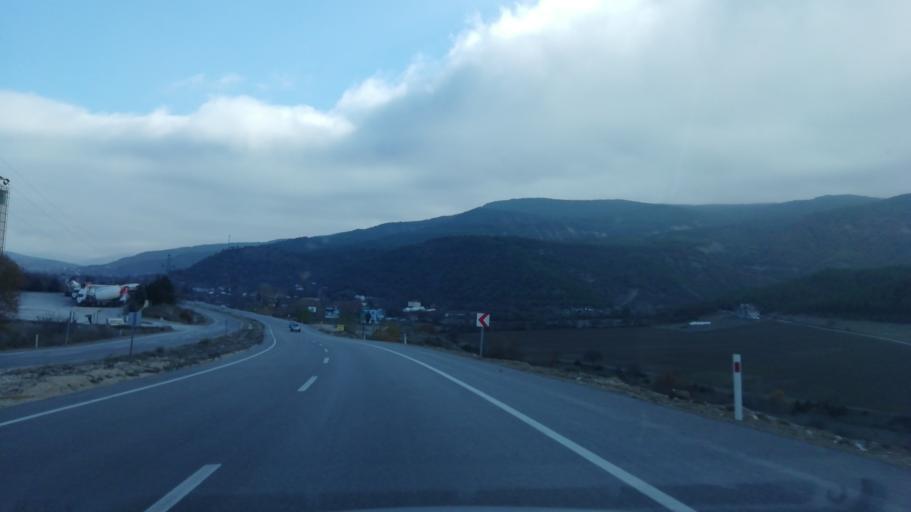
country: TR
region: Karabuk
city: Safranbolu
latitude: 41.2181
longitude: 32.7286
